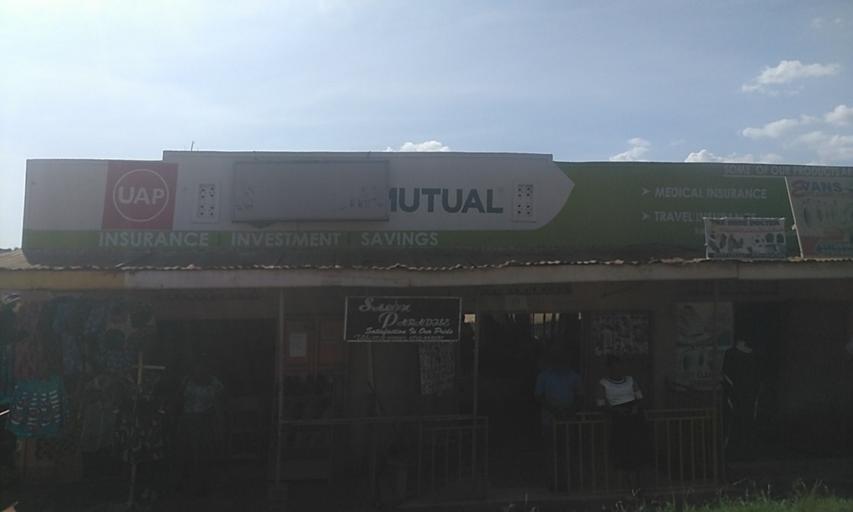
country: UG
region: Central Region
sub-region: Wakiso District
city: Kireka
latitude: 0.3629
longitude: 32.6239
